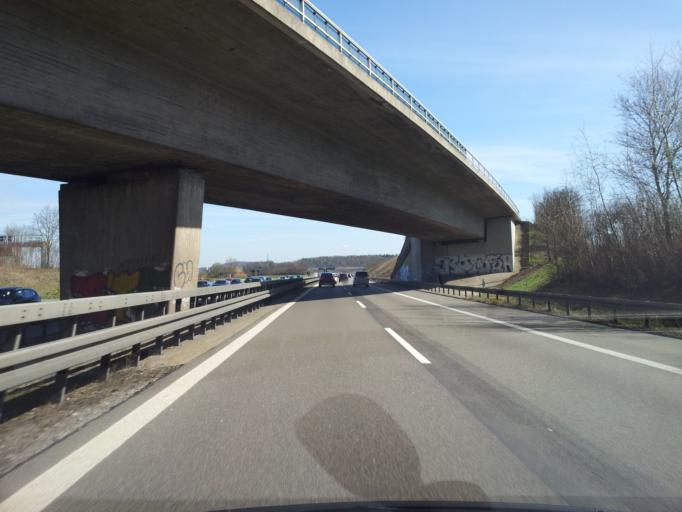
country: DE
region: Baden-Wuerttemberg
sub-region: Regierungsbezirk Stuttgart
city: Gartringen
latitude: 48.6369
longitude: 8.9222
